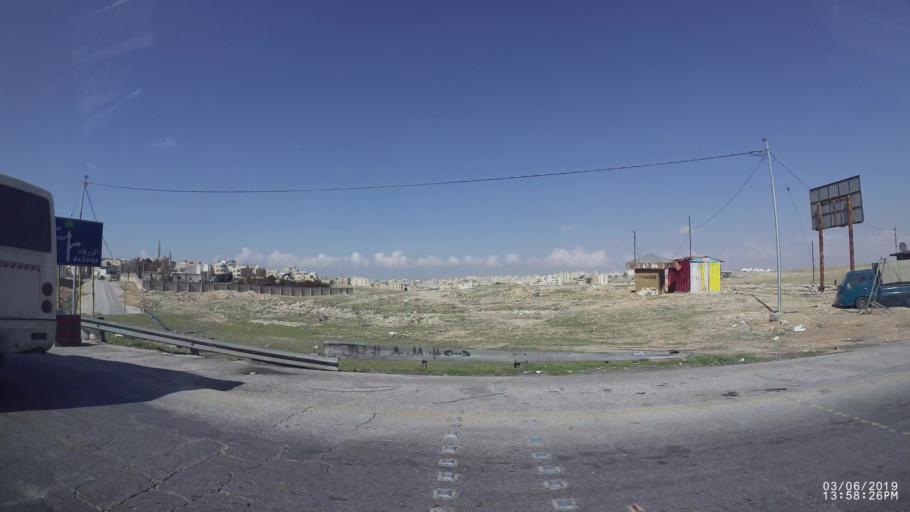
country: JO
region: Zarqa
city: Zarqa
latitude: 32.0273
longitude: 36.0911
